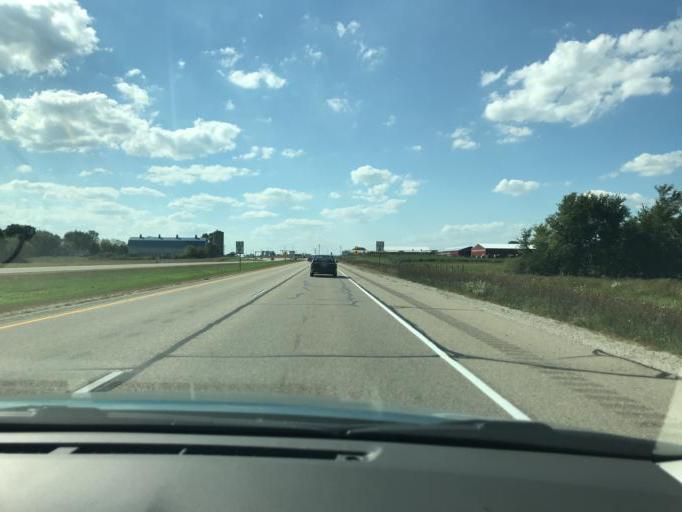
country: US
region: Wisconsin
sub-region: Kenosha County
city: Powers Lake
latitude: 42.5837
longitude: -88.2901
